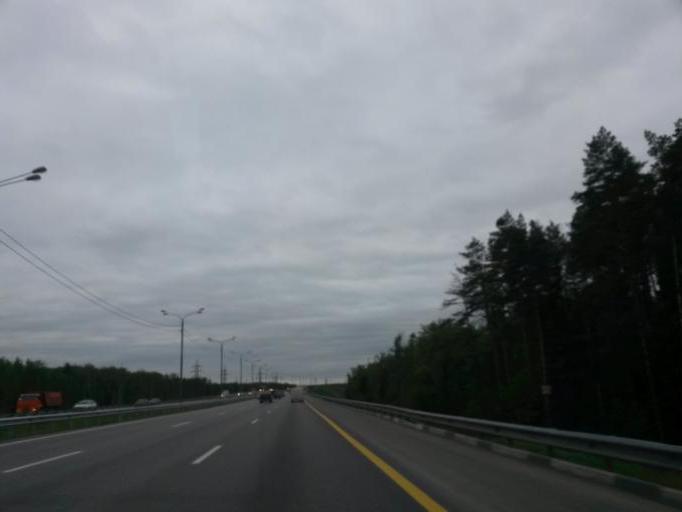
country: RU
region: Moskovskaya
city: Vostryakovo
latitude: 55.4236
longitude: 37.7967
